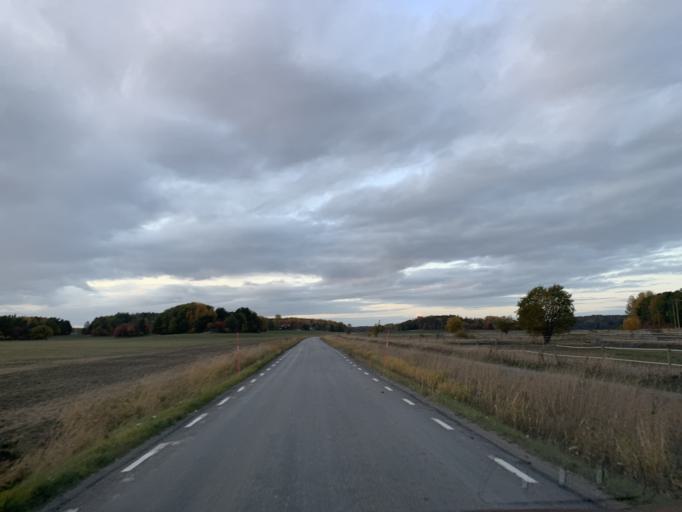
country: SE
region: Stockholm
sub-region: Nynashamns Kommun
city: Osmo
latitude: 58.9065
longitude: 17.7882
